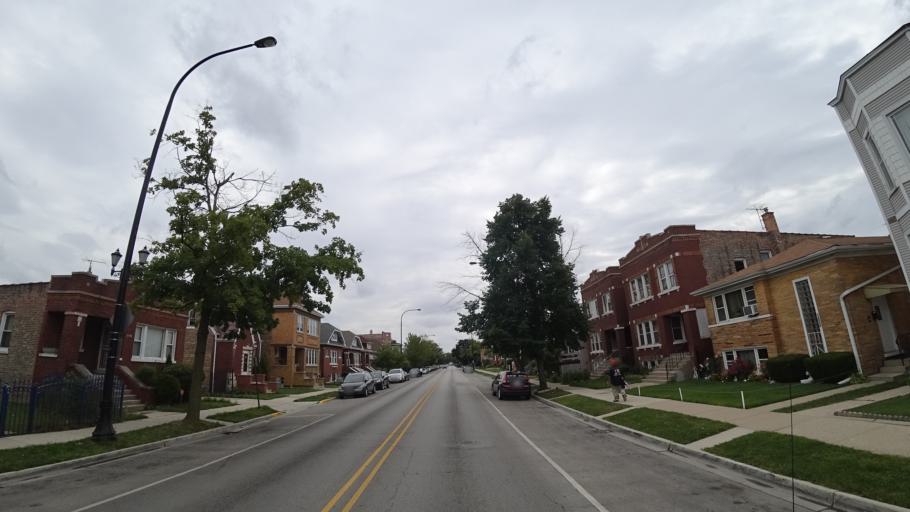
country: US
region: Illinois
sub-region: Cook County
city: Cicero
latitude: 41.8563
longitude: -87.7641
